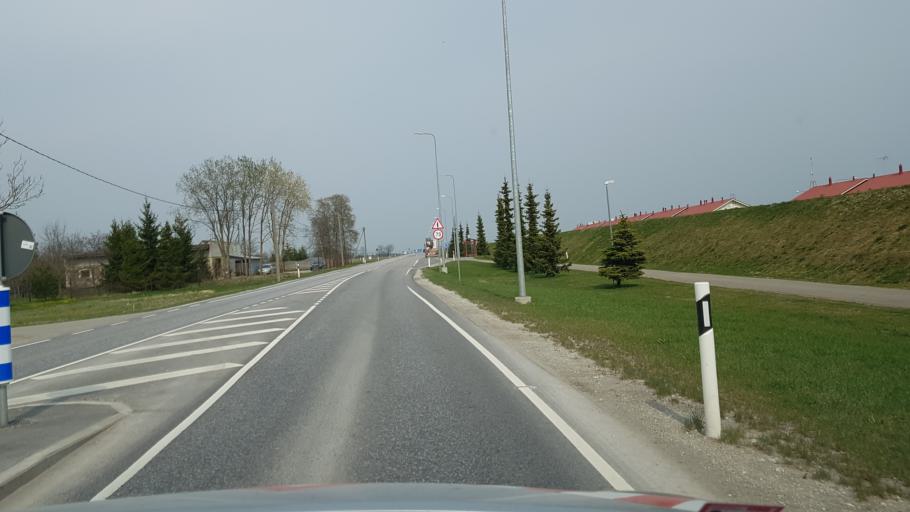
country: EE
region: Harju
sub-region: Kiili vald
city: Kiili
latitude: 59.3271
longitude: 24.8209
